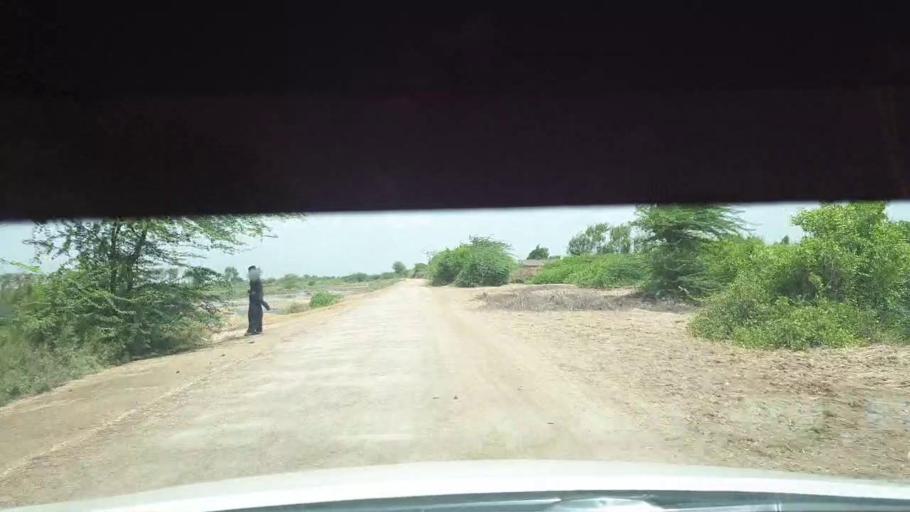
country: PK
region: Sindh
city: Kadhan
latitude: 24.5081
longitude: 68.9781
